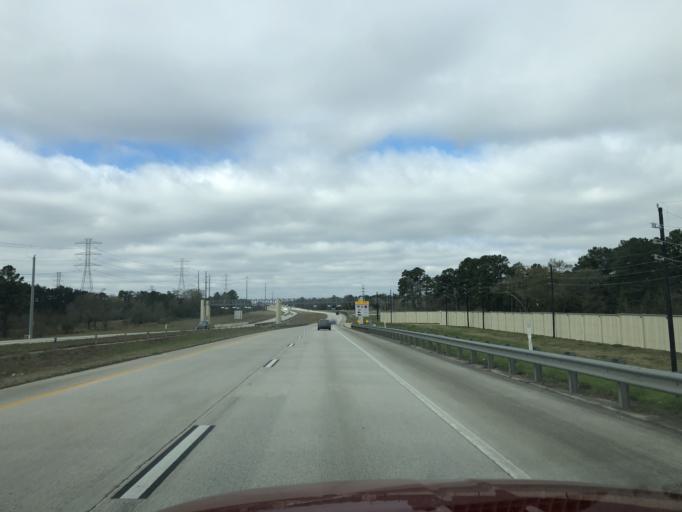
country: US
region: Texas
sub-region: Harris County
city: Spring
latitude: 30.0932
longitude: -95.4793
